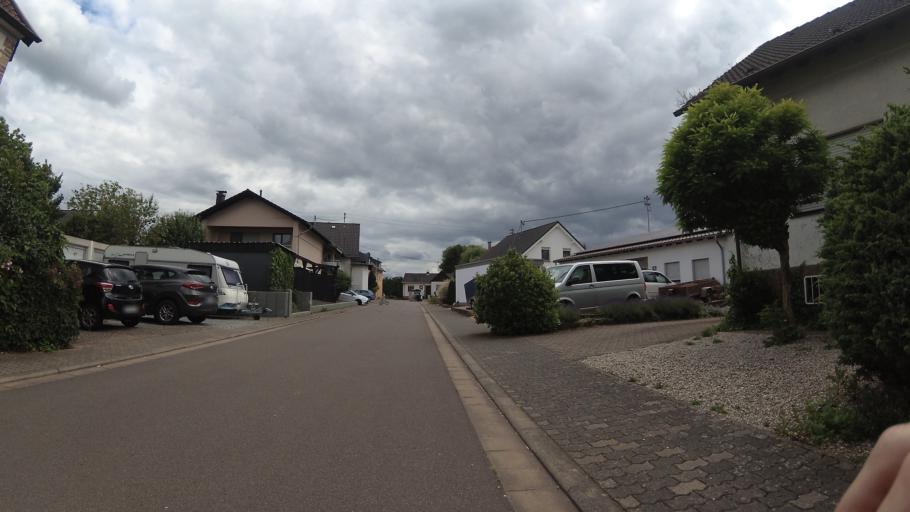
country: DE
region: Saarland
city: Nalbach
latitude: 49.3754
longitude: 6.7885
